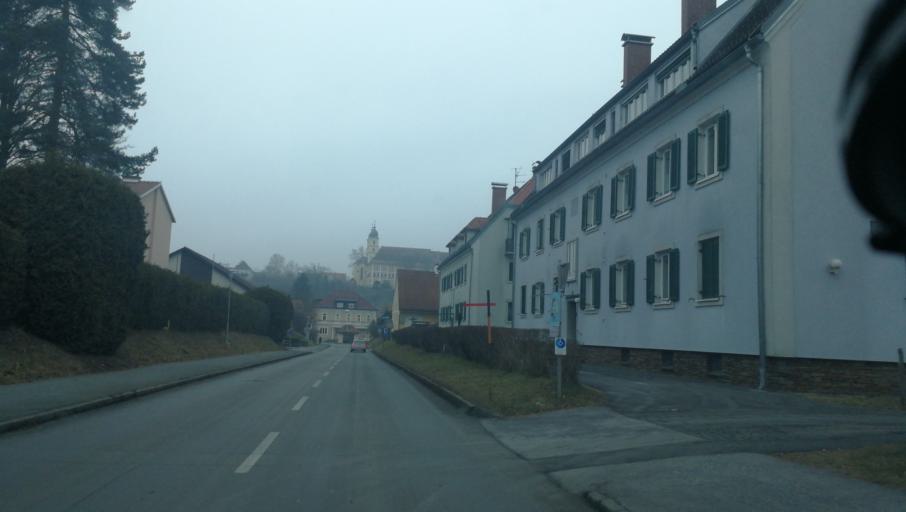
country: AT
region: Styria
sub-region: Politischer Bezirk Deutschlandsberg
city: Stainz
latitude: 46.8918
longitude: 15.2614
